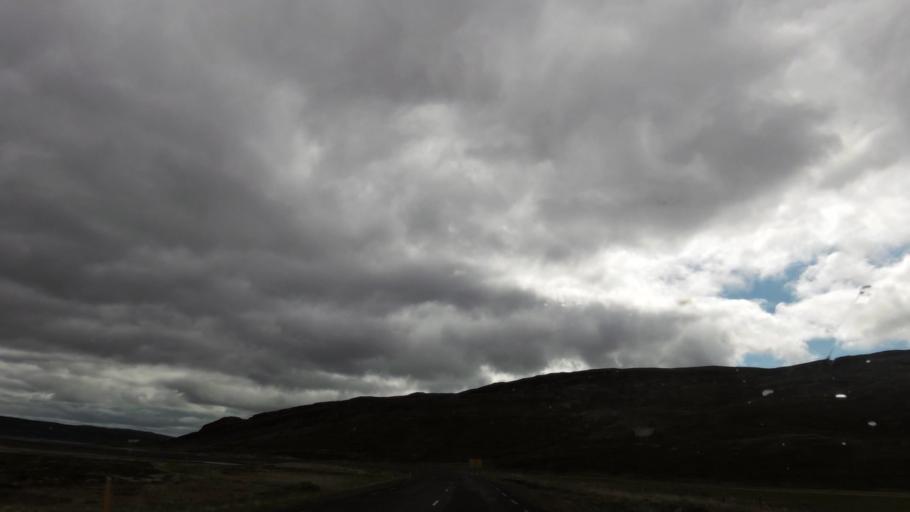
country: IS
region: West
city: Stykkisholmur
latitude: 65.7653
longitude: -21.7888
